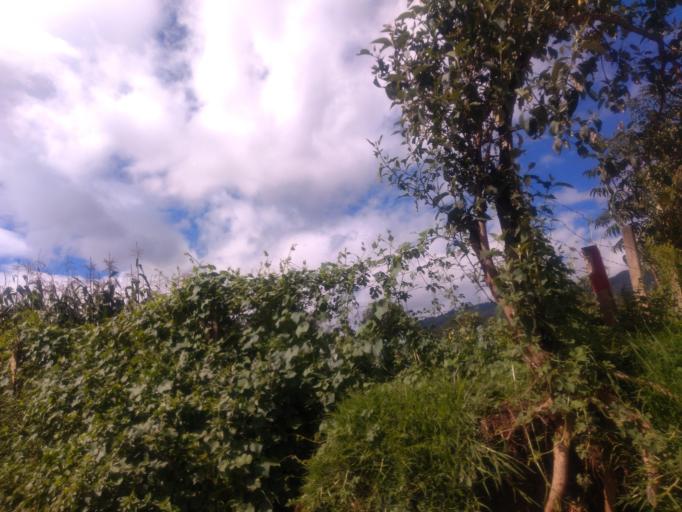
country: GT
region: Quetzaltenango
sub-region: Municipio de La Esperanza
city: La Esperanza
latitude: 14.8546
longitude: -91.5673
